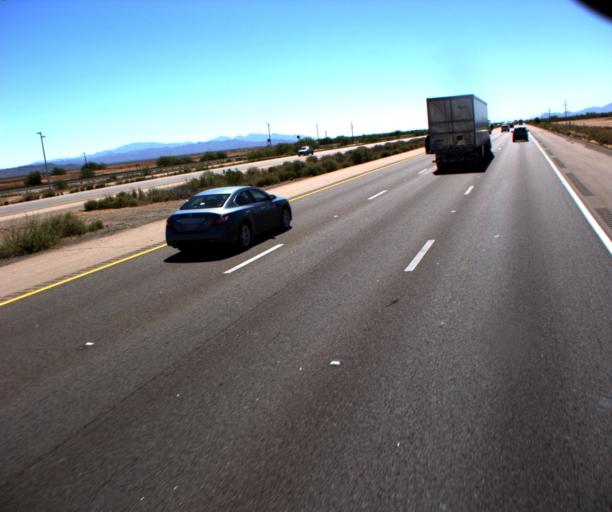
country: US
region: Arizona
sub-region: Pima County
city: Avra Valley
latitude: 32.6150
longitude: -111.3582
